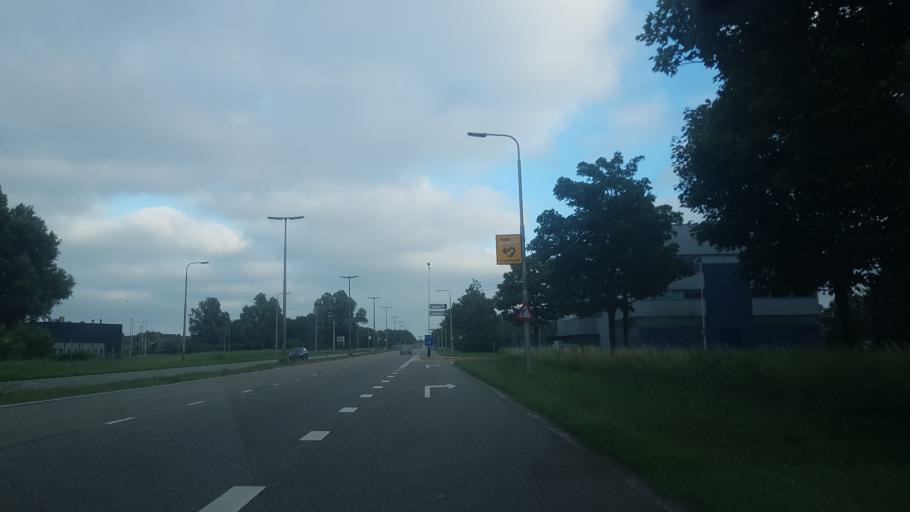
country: NL
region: Friesland
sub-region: Gemeente Leeuwarden
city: Camminghaburen
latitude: 53.2130
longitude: 5.8298
